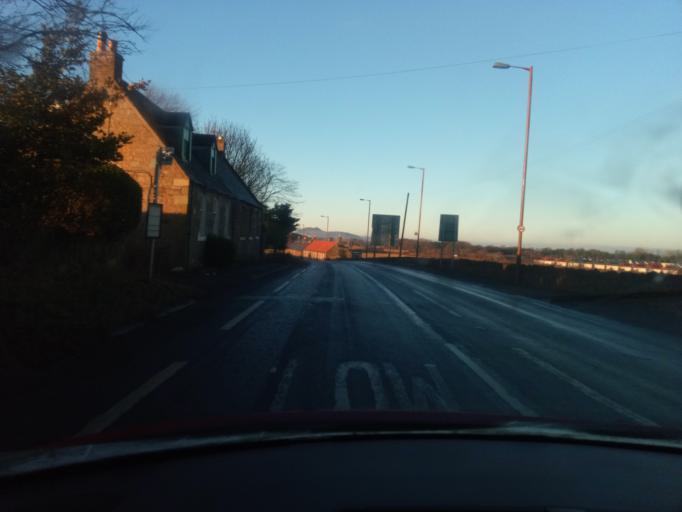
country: GB
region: Scotland
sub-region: East Lothian
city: Prestonpans
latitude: 55.9446
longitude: -2.9900
